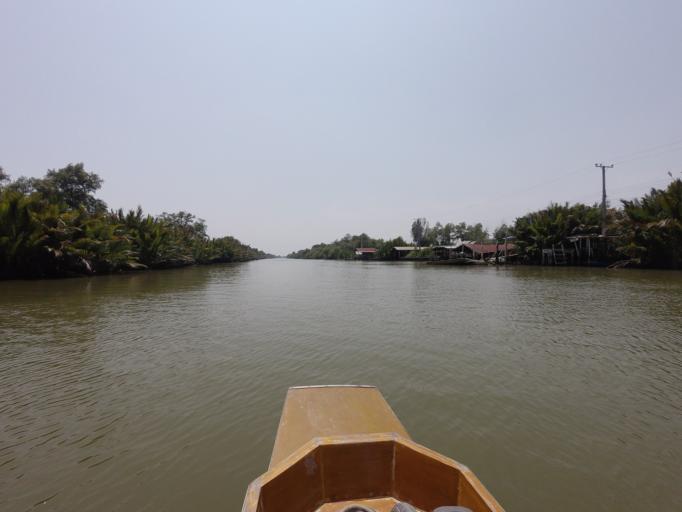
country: TH
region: Bangkok
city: Thung Khru
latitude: 13.5431
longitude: 100.4636
